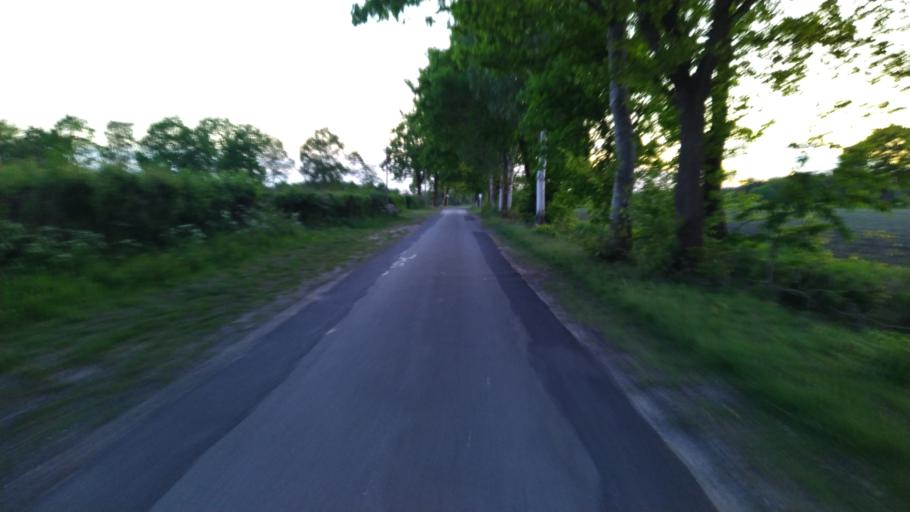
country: DE
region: Lower Saxony
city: Bargstedt
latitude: 53.4833
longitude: 9.4597
